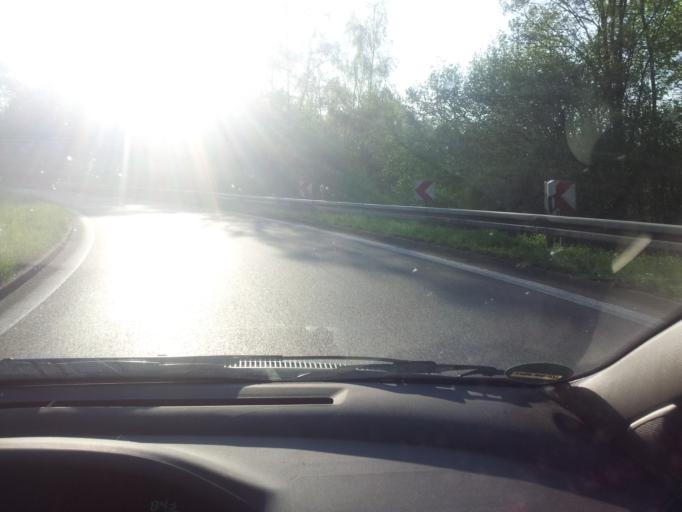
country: DE
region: Baden-Wuerttemberg
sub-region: Regierungsbezirk Stuttgart
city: Waiblingen
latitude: 48.8172
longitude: 9.3245
